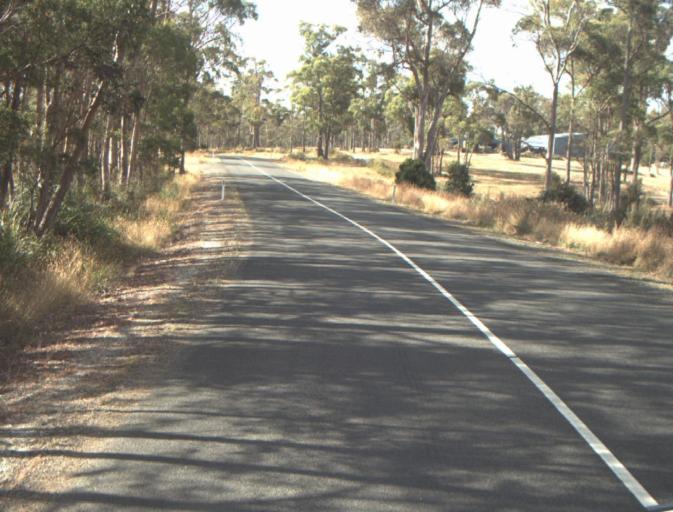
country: AU
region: Tasmania
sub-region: Dorset
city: Bridport
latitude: -41.1130
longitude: 147.2006
